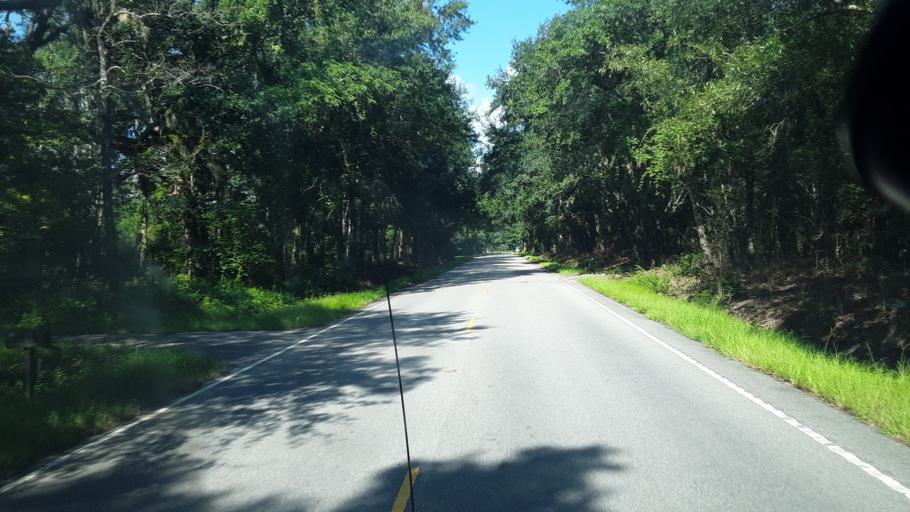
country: US
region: South Carolina
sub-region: Jasper County
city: Ridgeland
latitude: 32.5898
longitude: -80.9590
